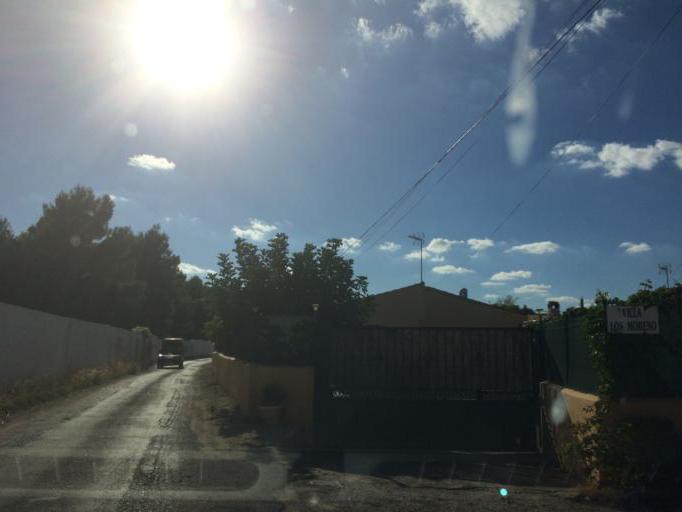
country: ES
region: Castille-La Mancha
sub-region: Provincia de Albacete
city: Albacete
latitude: 38.9936
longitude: -1.8821
